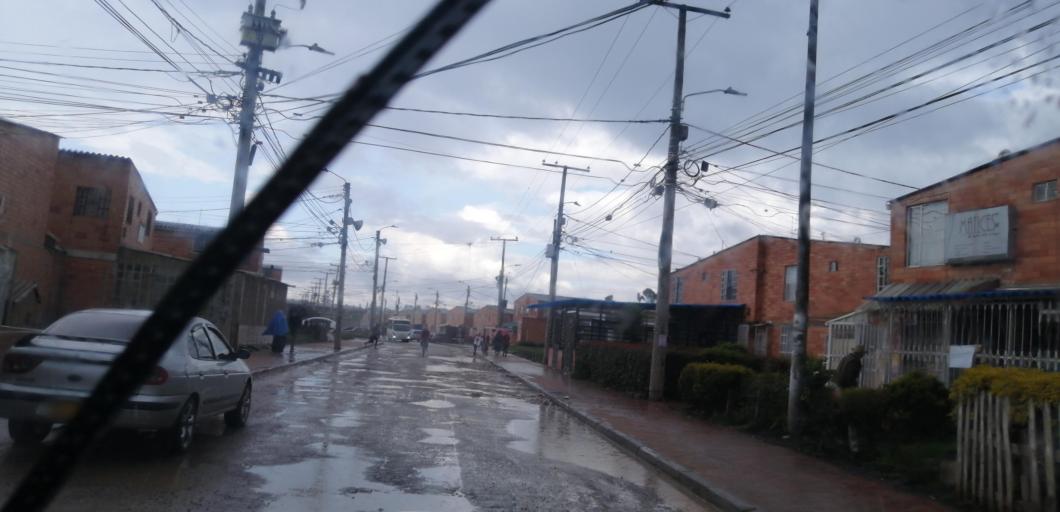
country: CO
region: Cundinamarca
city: Madrid
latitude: 4.7278
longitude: -74.2827
